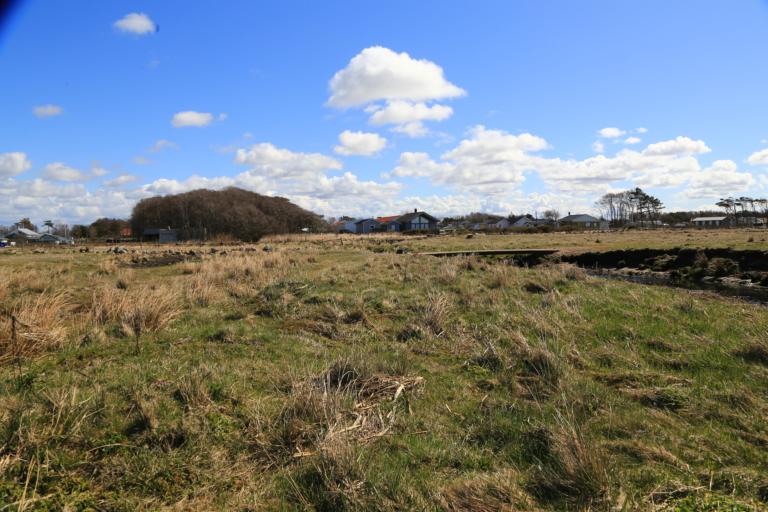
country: SE
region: Halland
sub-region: Varbergs Kommun
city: Traslovslage
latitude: 57.0672
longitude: 12.2766
